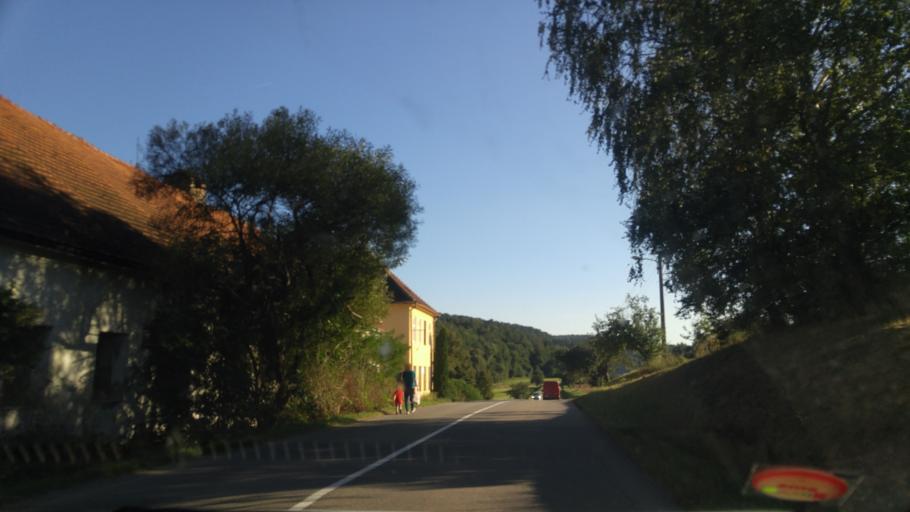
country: CZ
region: South Moravian
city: Veverska Bityska
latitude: 49.2500
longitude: 16.4481
